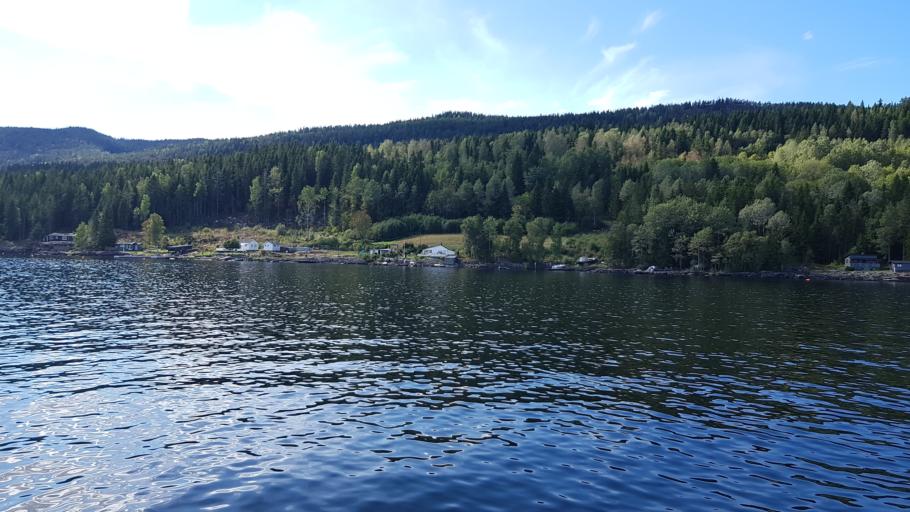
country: NO
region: Akershus
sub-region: Hurdal
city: Hurdal
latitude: 60.5449
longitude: 11.1984
